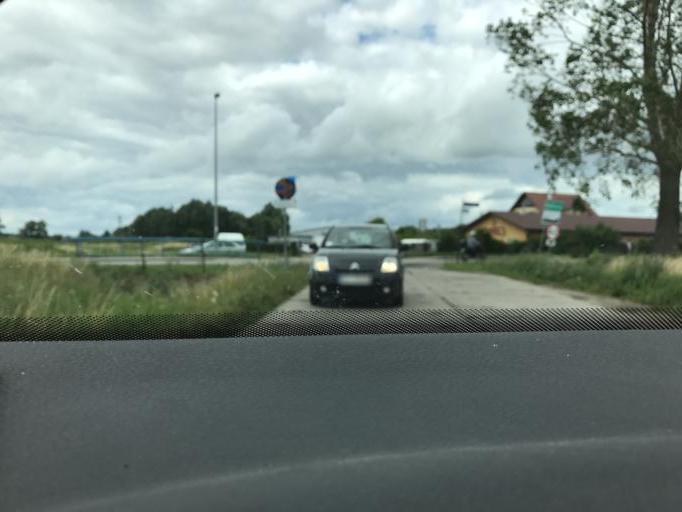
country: PL
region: Pomeranian Voivodeship
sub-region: Powiat gdanski
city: Pruszcz Gdanski
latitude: 54.2693
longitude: 18.6762
